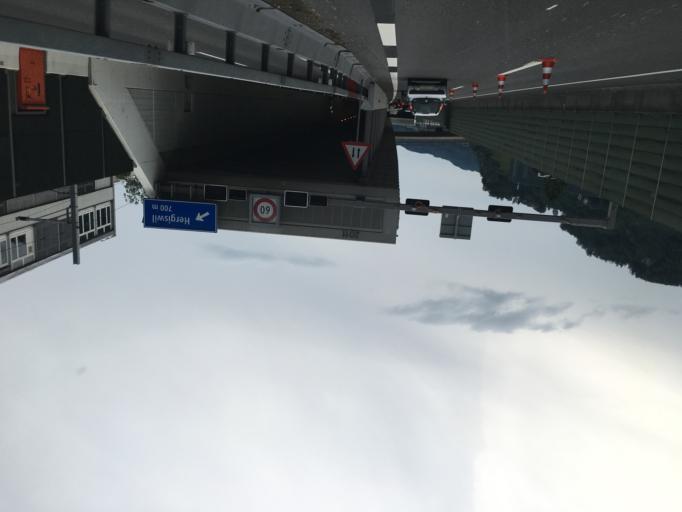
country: CH
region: Nidwalden
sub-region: Nidwalden
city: Stansstad
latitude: 46.9725
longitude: 8.3410
